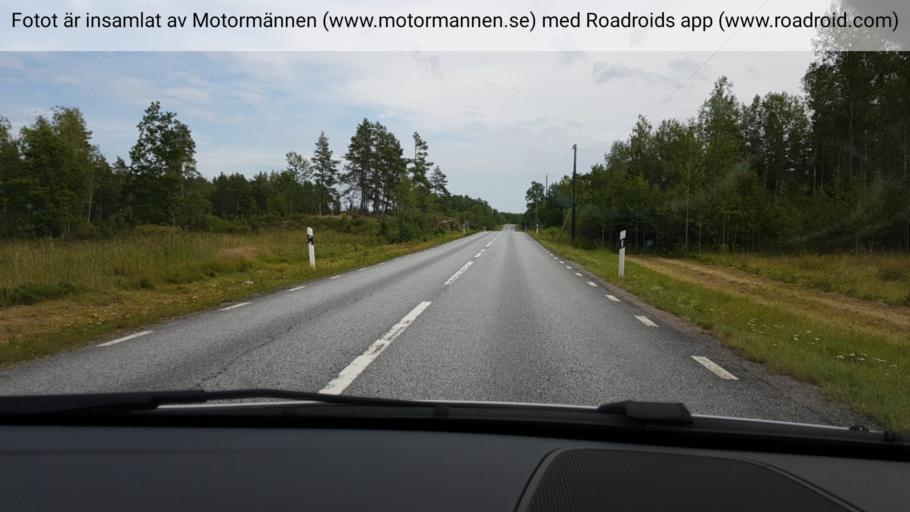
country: SE
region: Stockholm
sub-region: Norrtalje Kommun
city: Hallstavik
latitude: 60.0955
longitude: 18.4731
